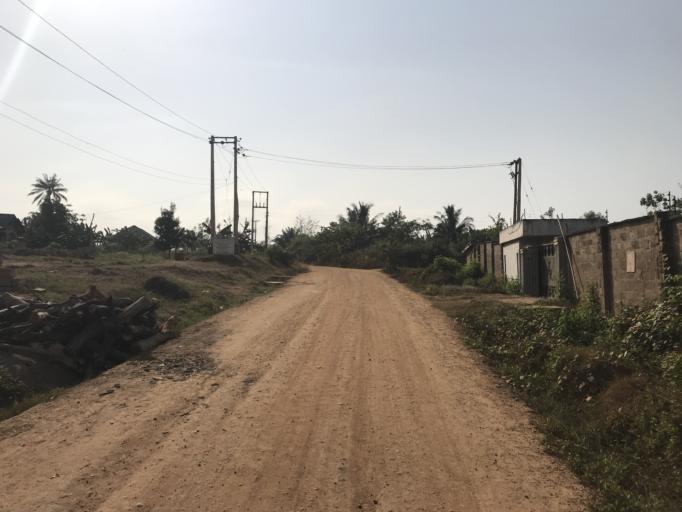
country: NG
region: Osun
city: Iwo
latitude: 7.6181
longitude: 4.1448
